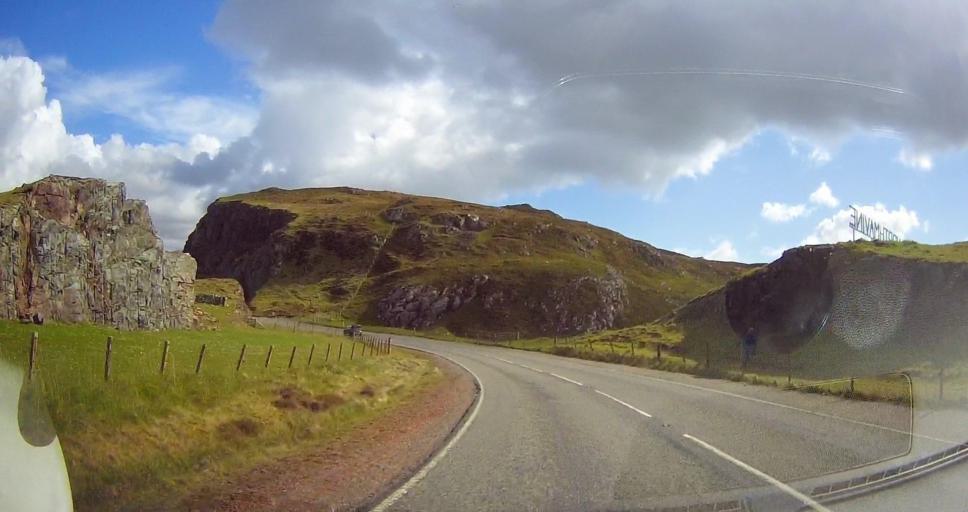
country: GB
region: Scotland
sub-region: Shetland Islands
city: Lerwick
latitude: 60.3990
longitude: -1.3851
